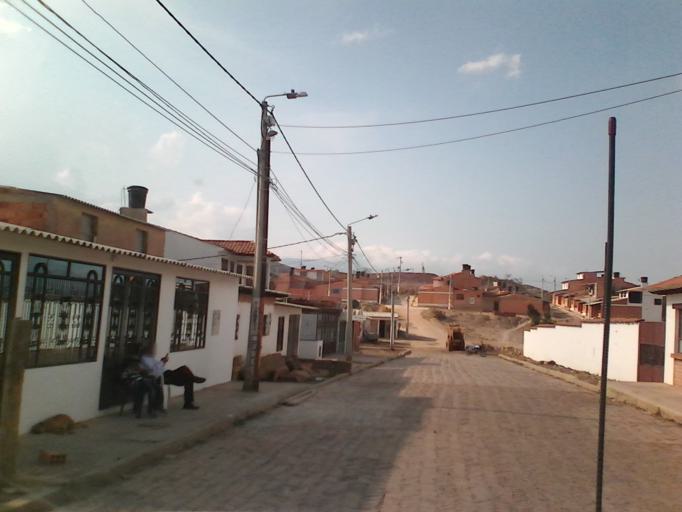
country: CO
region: Boyaca
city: Sachica
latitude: 5.5860
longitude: -73.5441
